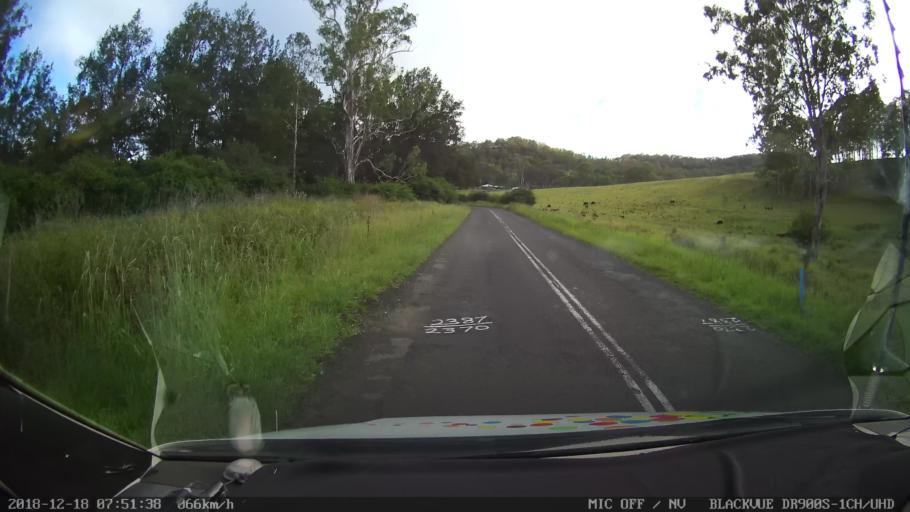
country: AU
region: New South Wales
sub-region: Kyogle
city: Kyogle
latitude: -28.4360
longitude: 152.5799
